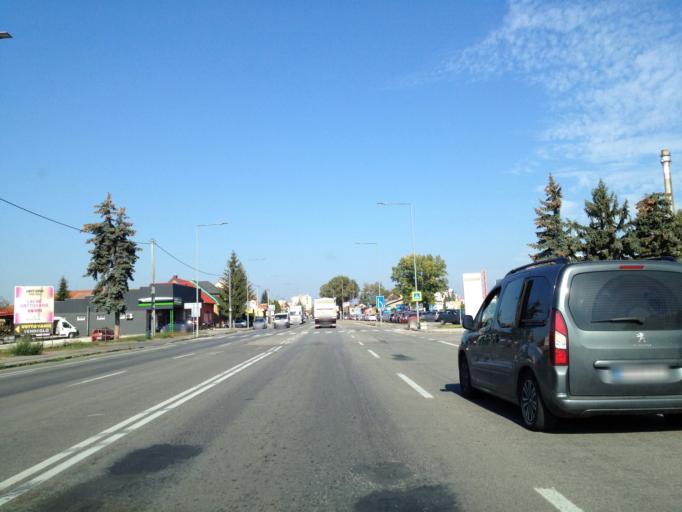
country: SK
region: Nitriansky
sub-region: Okres Nove Zamky
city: Nove Zamky
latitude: 47.9769
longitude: 18.1789
